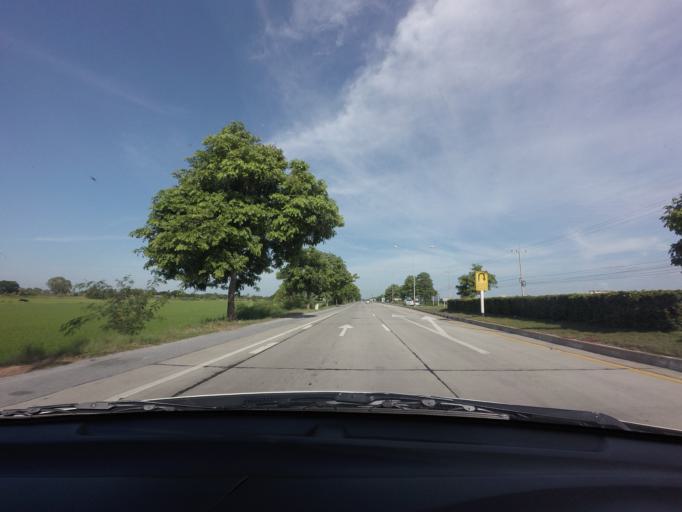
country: TH
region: Suphan Buri
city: Suphan Buri
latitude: 14.4614
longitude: 100.0515
